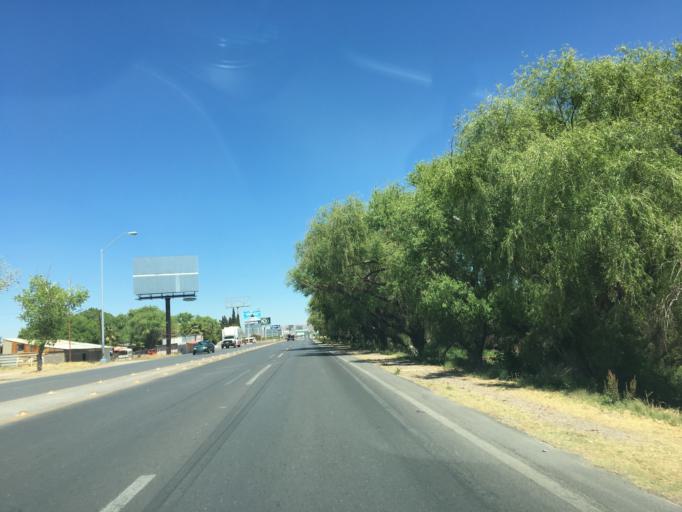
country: MX
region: Chihuahua
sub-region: Aquiles Serdan
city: Ninguno [CERESO]
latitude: 28.6967
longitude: -105.9816
